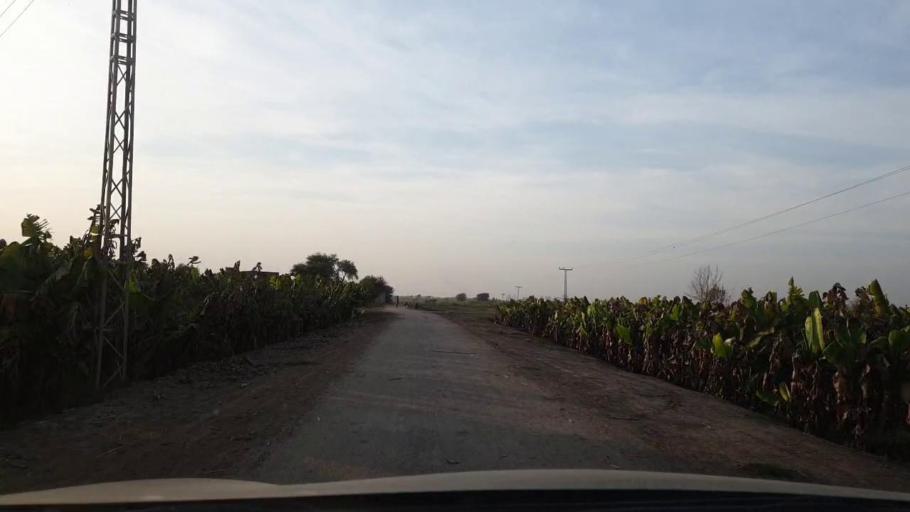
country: PK
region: Sindh
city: Tando Adam
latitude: 25.7148
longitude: 68.7251
